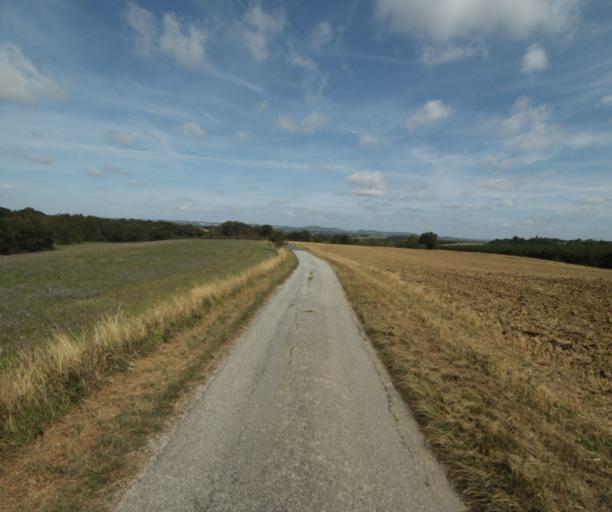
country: FR
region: Midi-Pyrenees
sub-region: Departement du Tarn
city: Soreze
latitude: 43.4746
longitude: 2.0984
